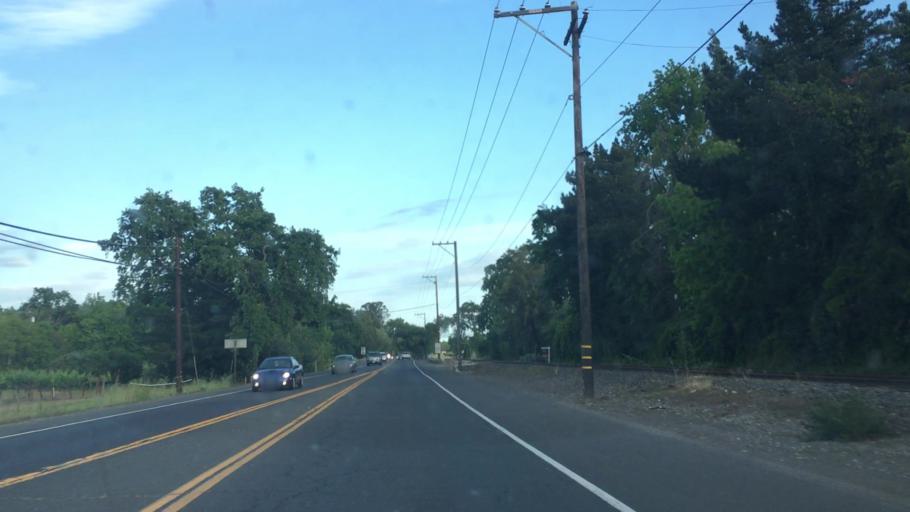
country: US
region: California
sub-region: Napa County
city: Yountville
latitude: 38.4334
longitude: -122.3996
